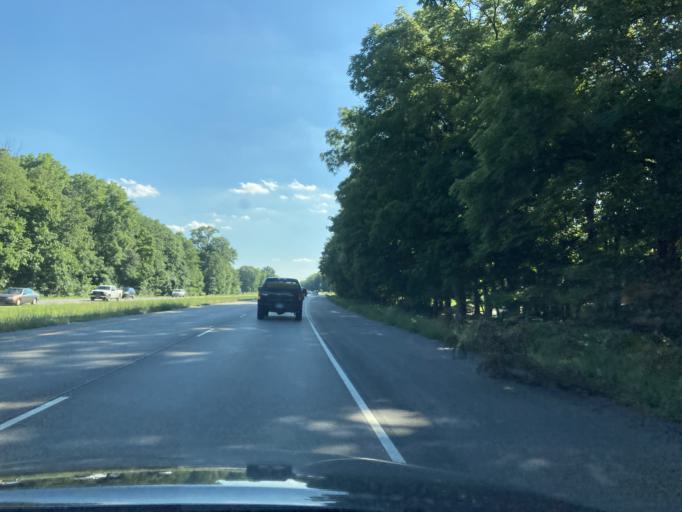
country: US
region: Indiana
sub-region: Marion County
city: Broad Ripple
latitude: 39.8514
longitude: -86.0996
